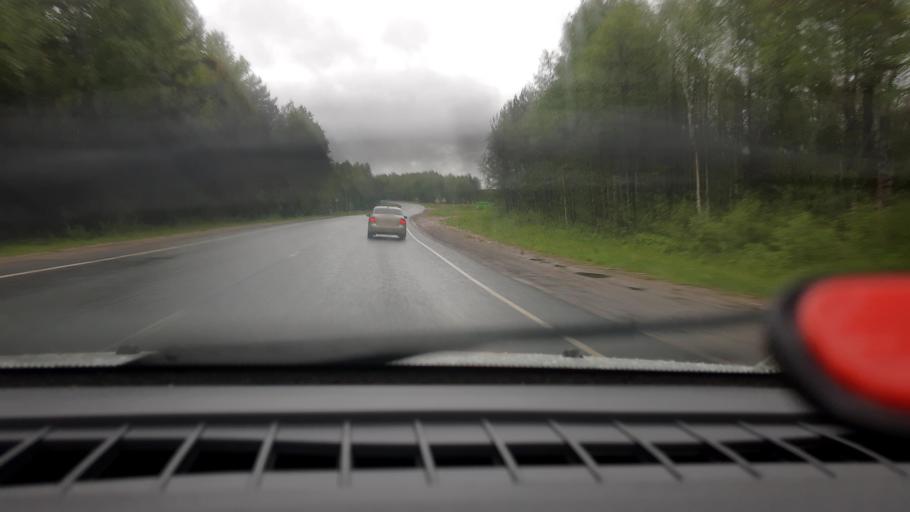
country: RU
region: Nizjnij Novgorod
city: Linda
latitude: 56.6653
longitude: 44.1332
